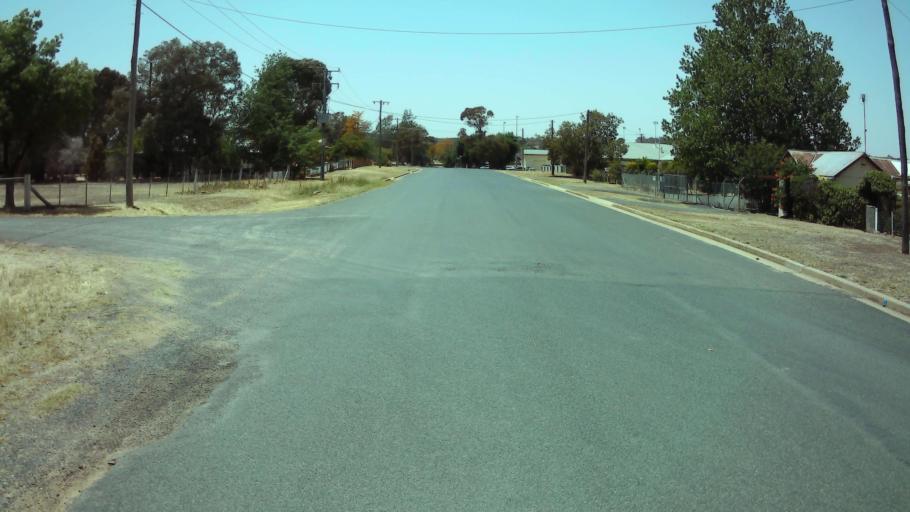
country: AU
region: New South Wales
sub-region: Weddin
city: Grenfell
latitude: -33.8902
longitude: 148.1590
